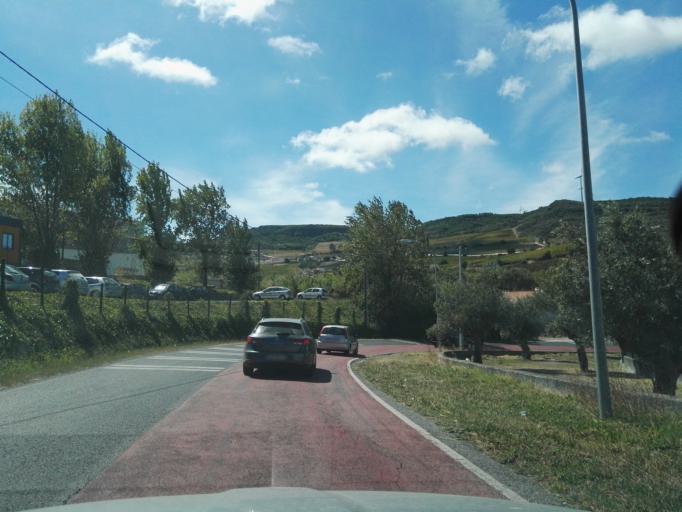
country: PT
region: Lisbon
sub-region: Arruda Dos Vinhos
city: Arruda dos Vinhos
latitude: 38.9773
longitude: -9.0728
